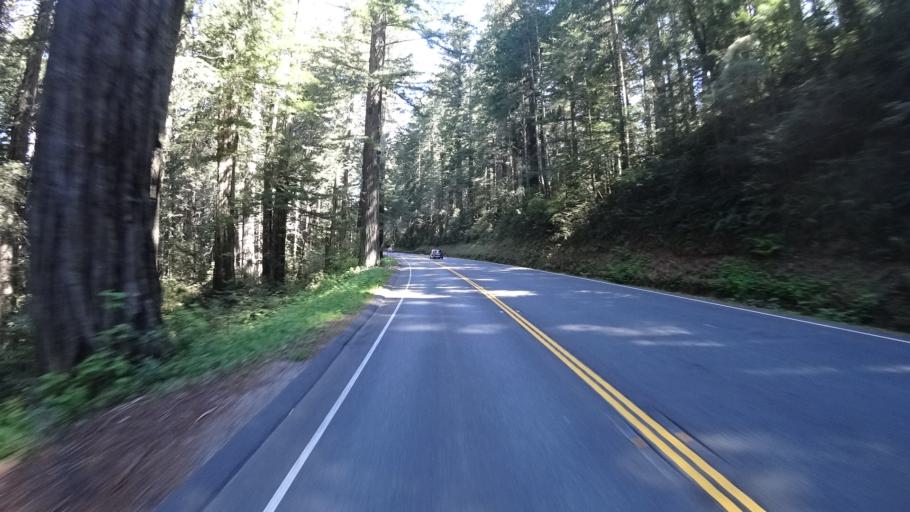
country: US
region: California
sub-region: Del Norte County
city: Bertsch-Oceanview
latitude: 41.6665
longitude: -124.1129
